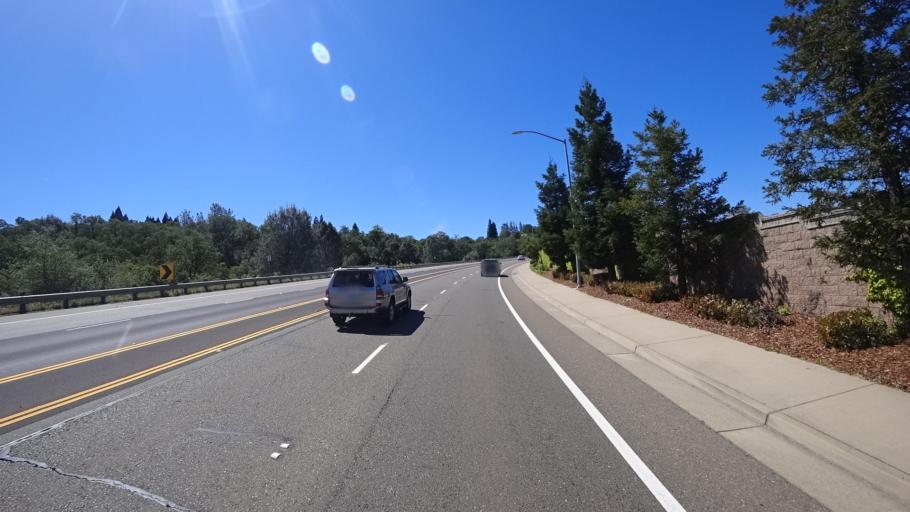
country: US
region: California
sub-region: Placer County
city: Rocklin
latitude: 38.7781
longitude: -121.2028
